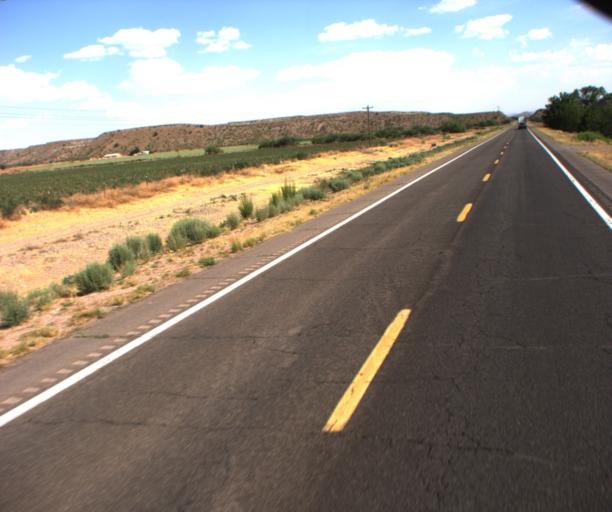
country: US
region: Arizona
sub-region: Greenlee County
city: Clifton
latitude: 32.8524
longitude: -109.1820
